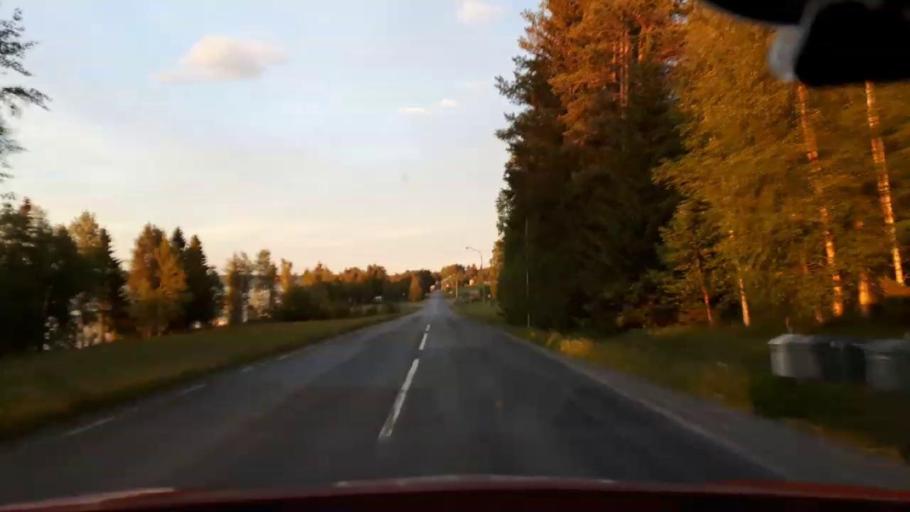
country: SE
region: Jaemtland
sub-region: OEstersunds Kommun
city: Ostersund
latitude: 63.1362
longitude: 14.6381
